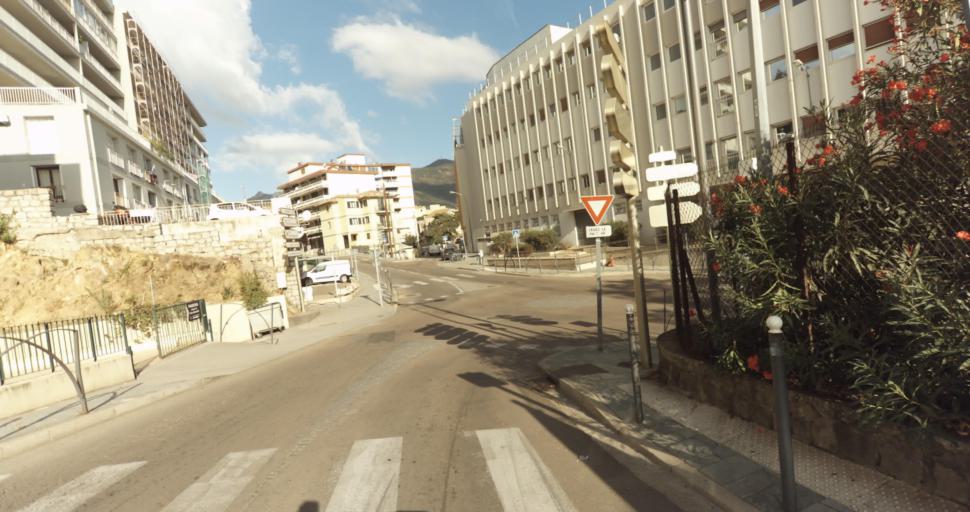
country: FR
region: Corsica
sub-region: Departement de la Corse-du-Sud
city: Ajaccio
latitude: 41.9283
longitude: 8.7348
